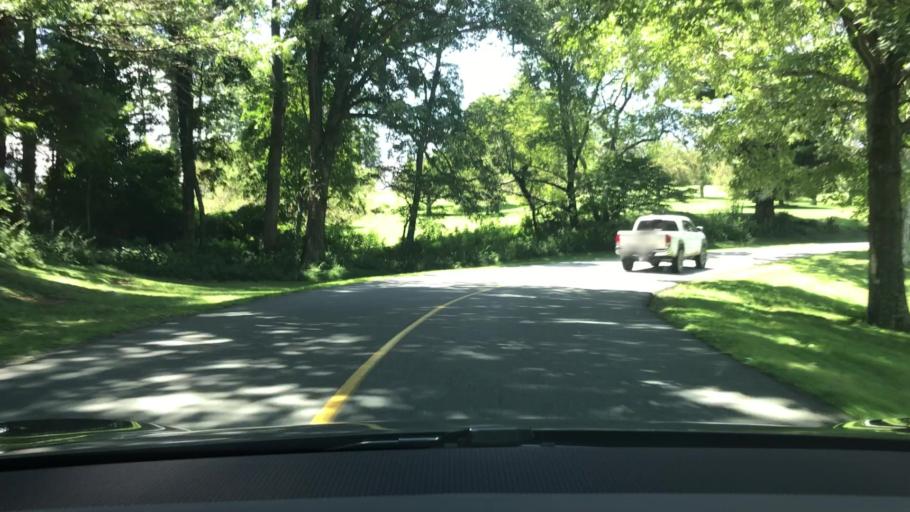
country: US
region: North Carolina
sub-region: Buncombe County
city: Asheville
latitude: 35.5569
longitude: -82.5744
